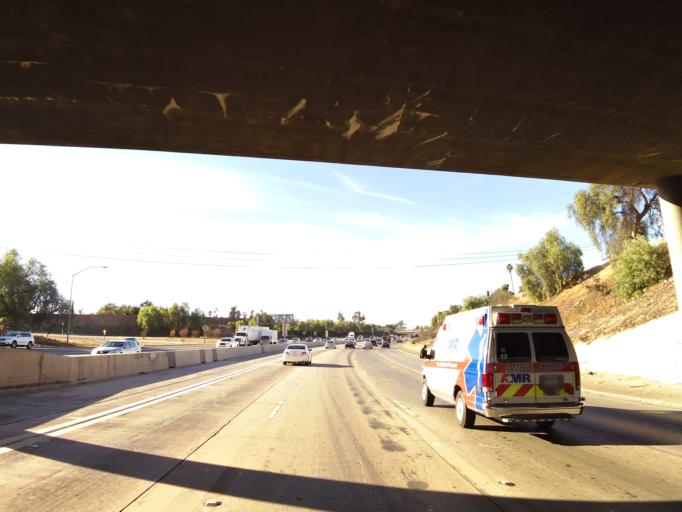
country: US
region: California
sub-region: Los Angeles County
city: North Hollywood
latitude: 34.2267
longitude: -118.3879
